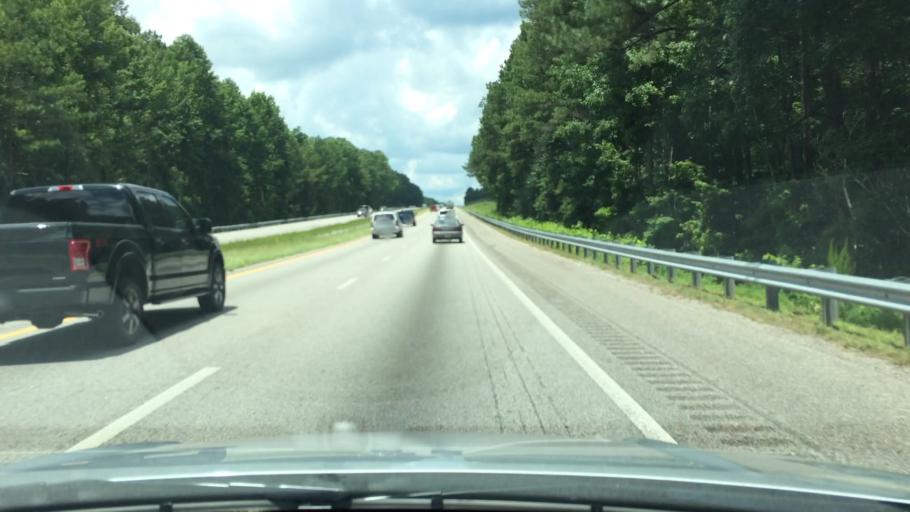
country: US
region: South Carolina
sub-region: Laurens County
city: Joanna
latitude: 34.4583
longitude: -81.7915
